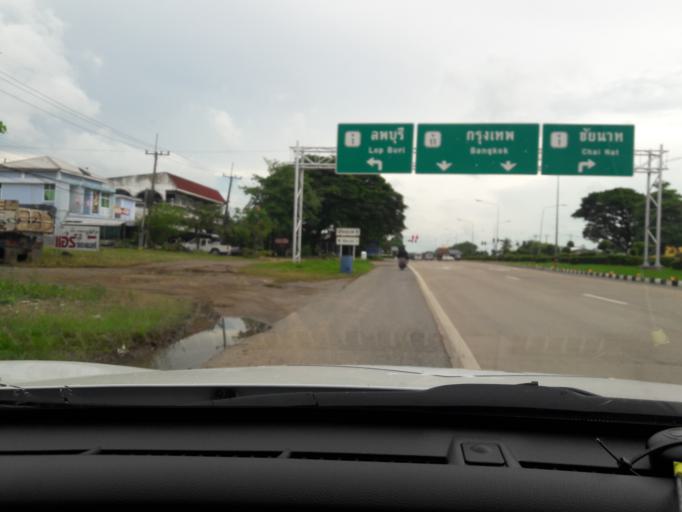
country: TH
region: Nakhon Sawan
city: Tak Fa
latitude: 15.3535
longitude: 100.5028
